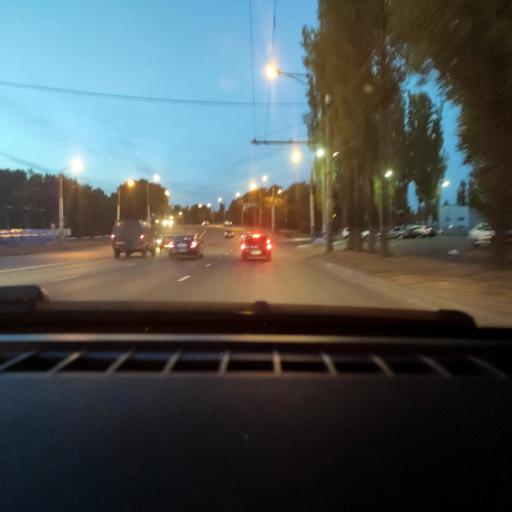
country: RU
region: Voronezj
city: Maslovka
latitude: 51.6204
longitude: 39.2364
